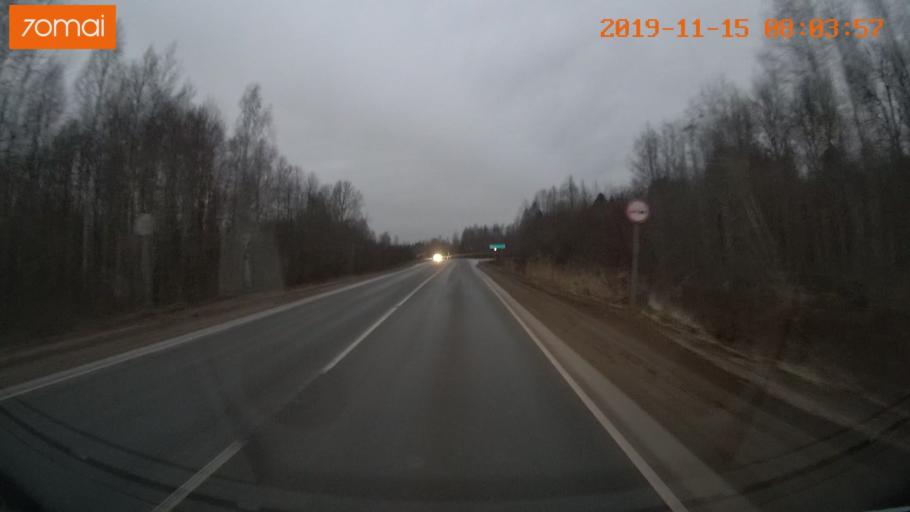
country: RU
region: Vologda
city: Cherepovets
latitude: 59.0033
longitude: 38.0829
